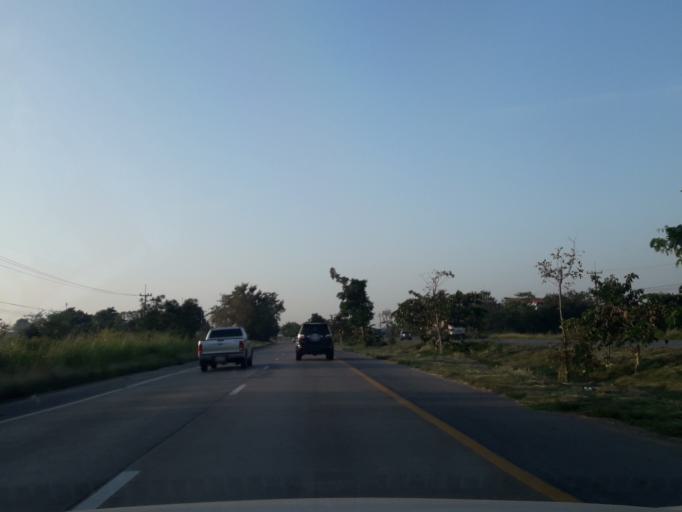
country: TH
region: Phra Nakhon Si Ayutthaya
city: Phra Nakhon Si Ayutthaya
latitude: 14.2958
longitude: 100.5246
